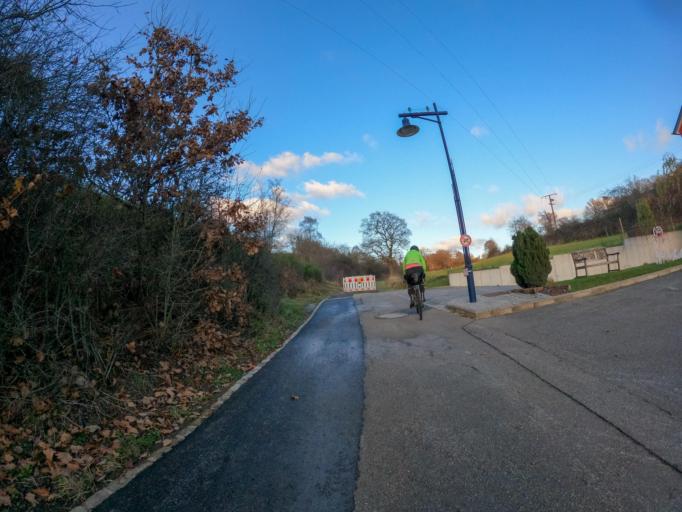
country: LU
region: Diekirch
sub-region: Canton de Wiltz
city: Bavigne
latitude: 49.9231
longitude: 5.8482
